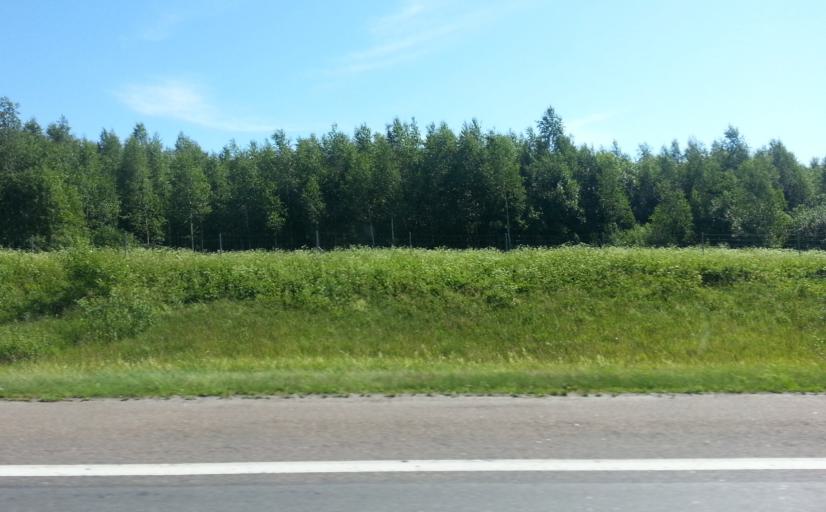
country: LT
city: Sirvintos
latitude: 55.1231
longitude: 24.8415
